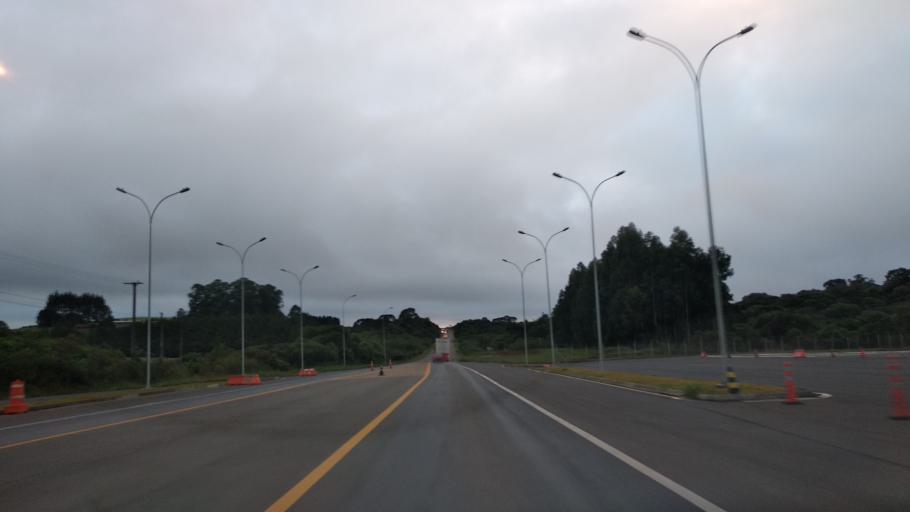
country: BR
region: Santa Catarina
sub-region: Campos Novos
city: Campos Novos
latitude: -27.3872
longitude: -51.1137
